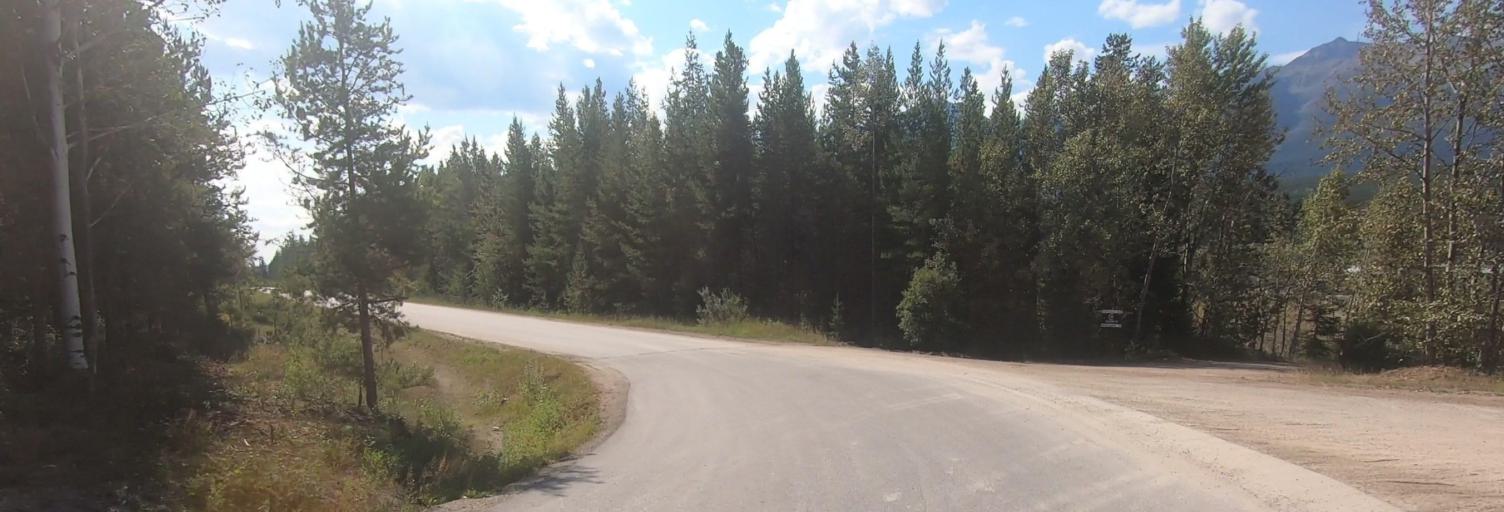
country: CA
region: British Columbia
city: Golden
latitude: 51.4928
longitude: -117.1761
